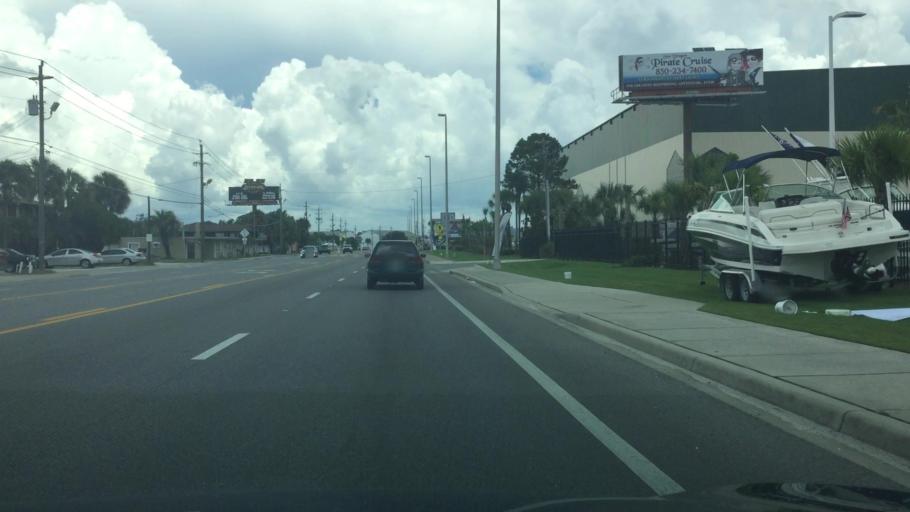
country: US
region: Florida
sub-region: Bay County
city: Lower Grand Lagoon
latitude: 30.1412
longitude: -85.7495
